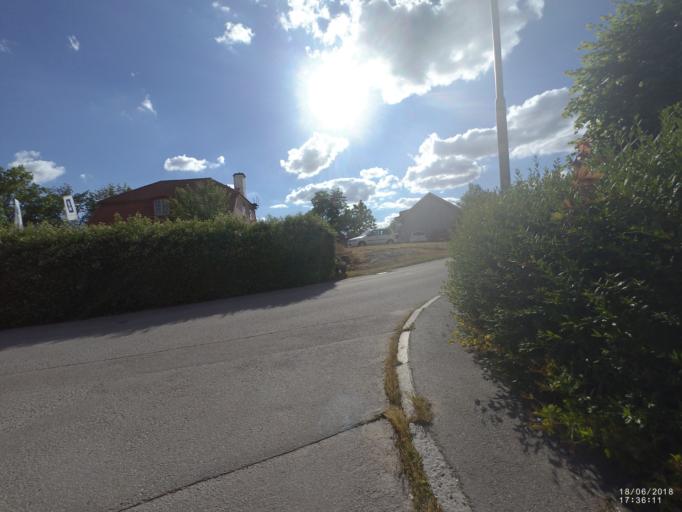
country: SE
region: Soedermanland
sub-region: Nykopings Kommun
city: Nykoping
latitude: 58.7574
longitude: 17.0100
